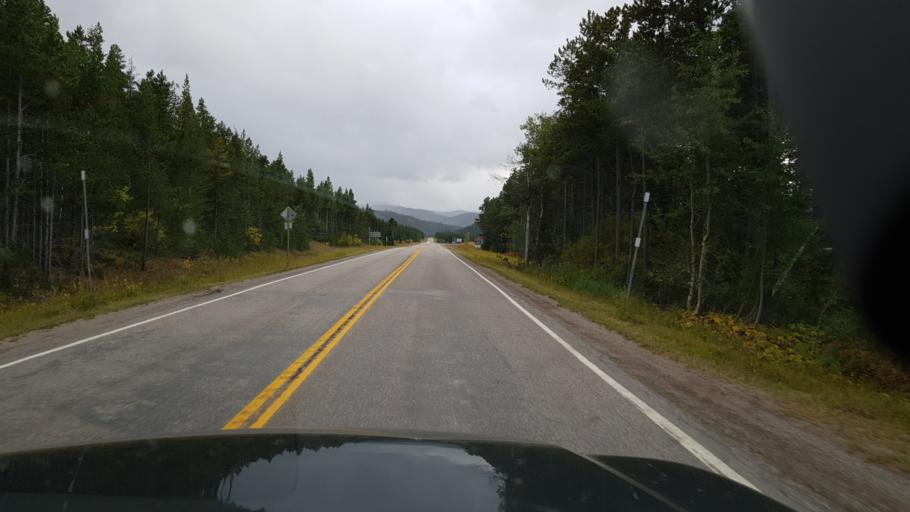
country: US
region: Montana
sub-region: Glacier County
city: South Browning
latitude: 48.3224
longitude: -113.3494
